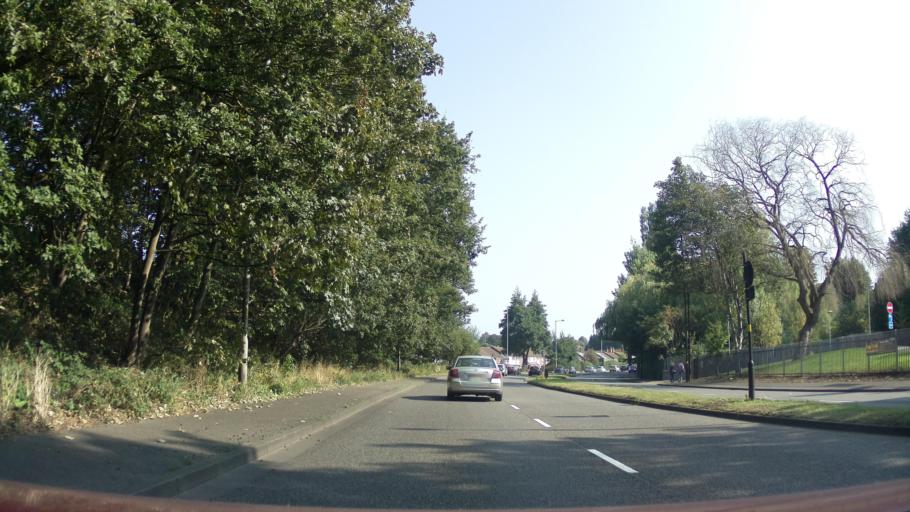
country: GB
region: England
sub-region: Walsall
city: Streetly
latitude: 52.5509
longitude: -1.9134
